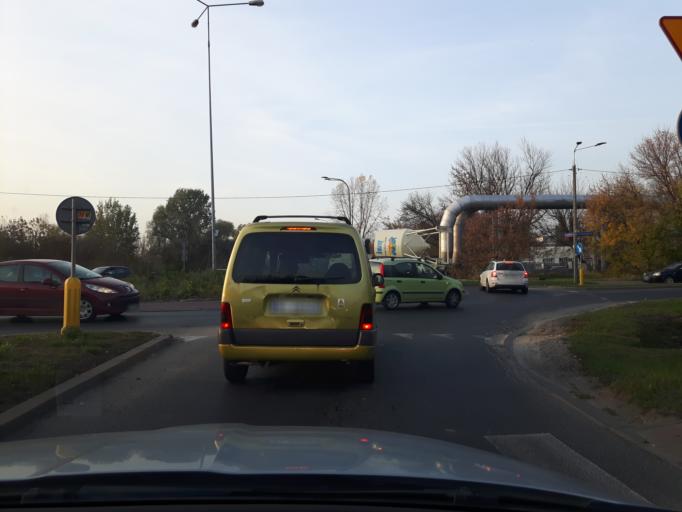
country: PL
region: Masovian Voivodeship
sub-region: Warszawa
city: Praga Poludnie
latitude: 52.2676
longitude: 21.0732
